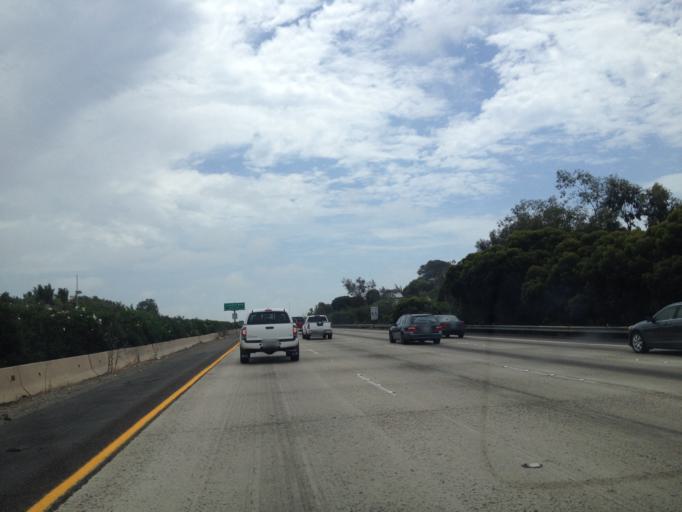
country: US
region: California
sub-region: San Diego County
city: Encinitas
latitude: 33.0751
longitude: -117.2953
